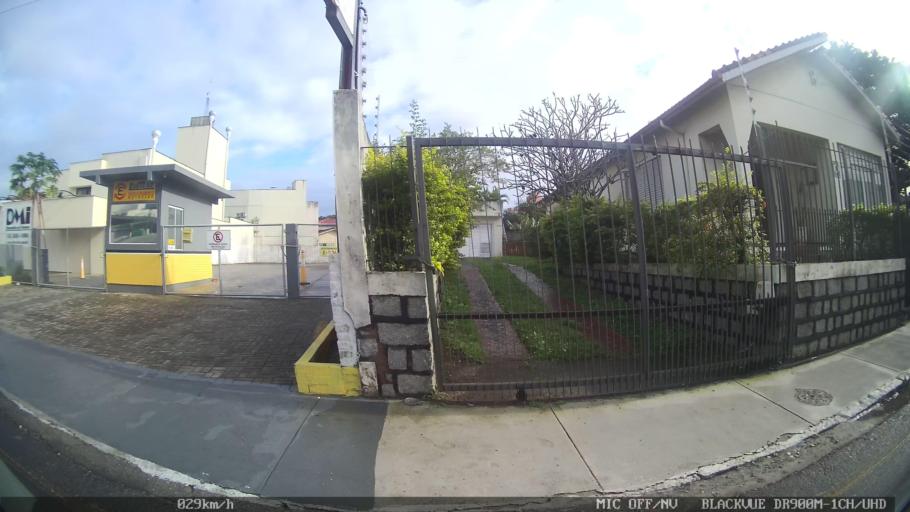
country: BR
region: Santa Catarina
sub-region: Sao Jose
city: Campinas
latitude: -27.6061
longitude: -48.6258
